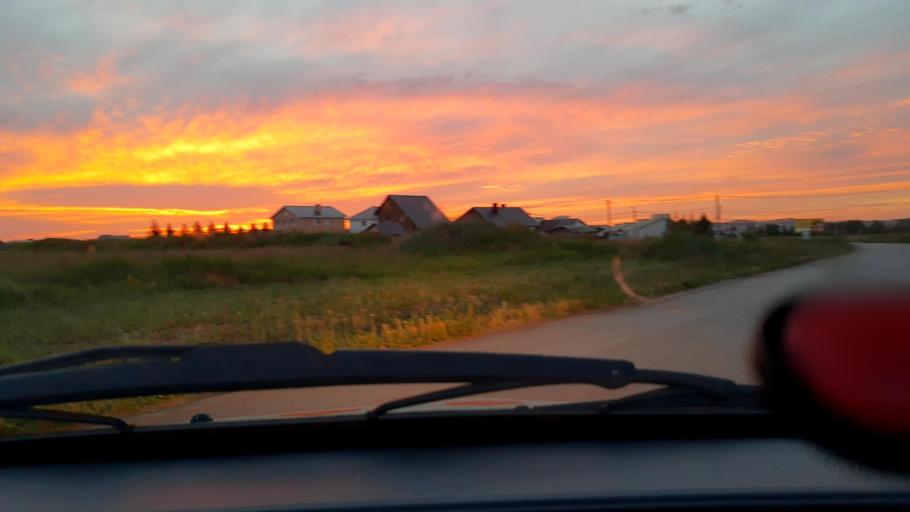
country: RU
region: Bashkortostan
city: Avdon
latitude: 54.4847
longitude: 55.8809
